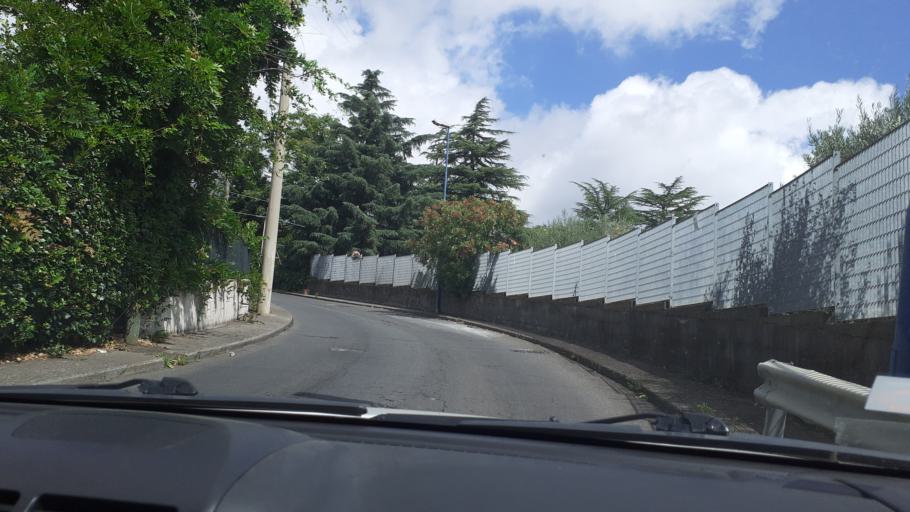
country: IT
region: Sicily
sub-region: Catania
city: Pedara
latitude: 37.6120
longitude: 15.0579
